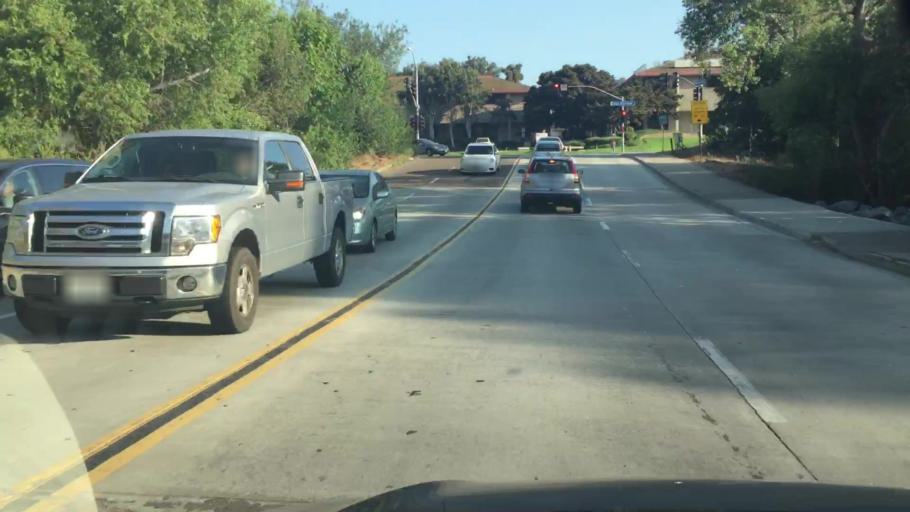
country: US
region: California
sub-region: San Diego County
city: San Diego
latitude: 32.7666
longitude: -117.1644
